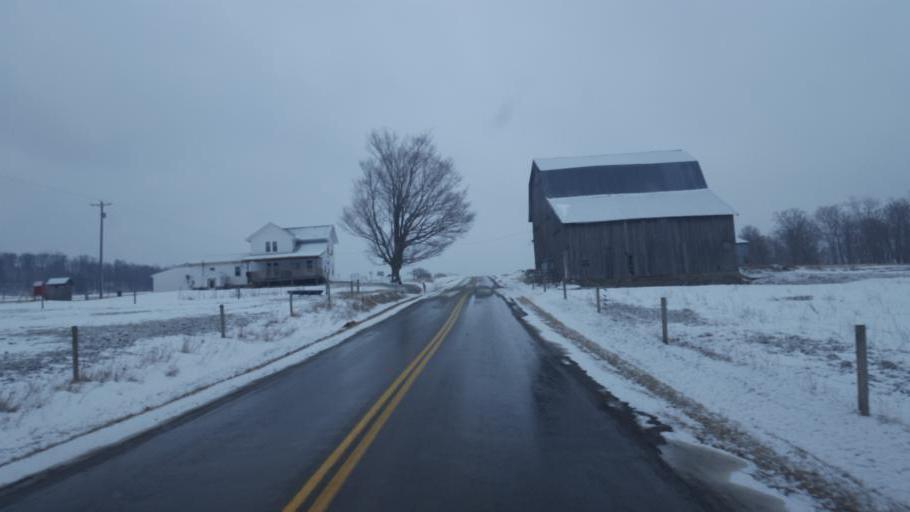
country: US
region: Pennsylvania
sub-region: Tioga County
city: Elkland
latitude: 42.0816
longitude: -77.4378
